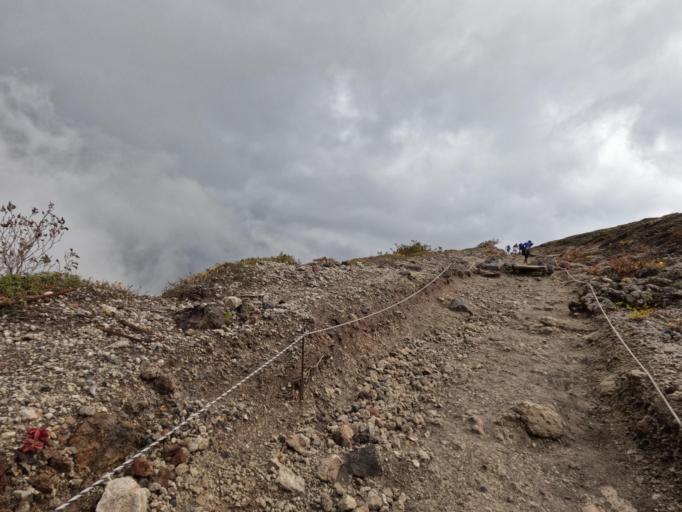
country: JP
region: Hokkaido
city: Shiraoi
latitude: 42.6938
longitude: 141.3902
